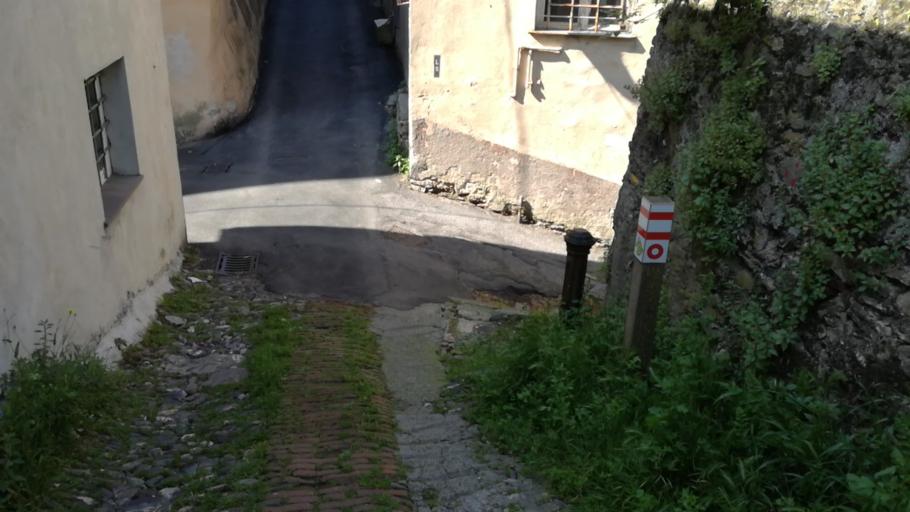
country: IT
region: Liguria
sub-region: Provincia di Genova
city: San Teodoro
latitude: 44.4224
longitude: 8.8974
